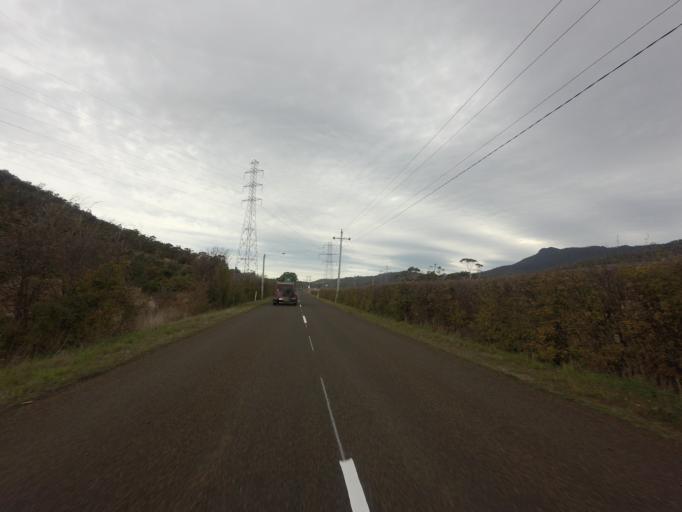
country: AU
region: Tasmania
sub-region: Brighton
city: Bridgewater
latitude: -42.6615
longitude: 147.1284
